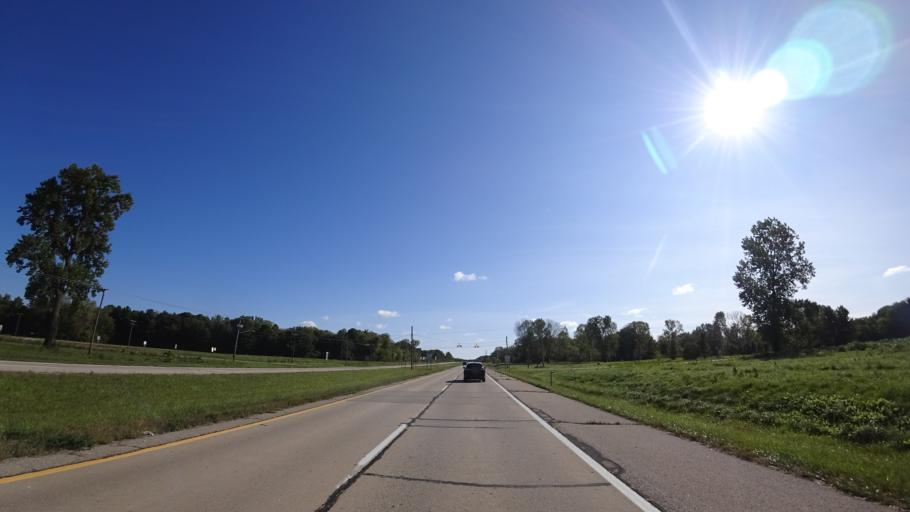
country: US
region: Michigan
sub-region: Berrien County
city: Benton Heights
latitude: 42.1191
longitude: -86.4187
